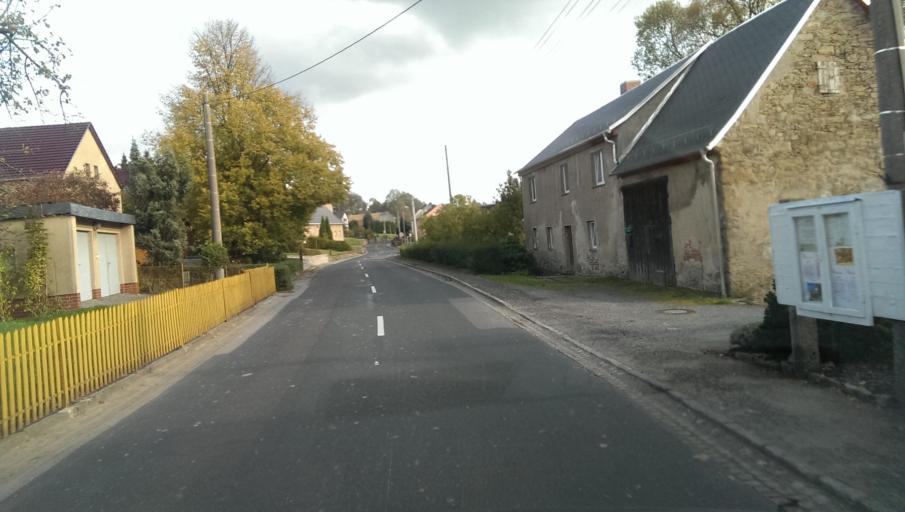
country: DE
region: Saxony
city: Haselbachtal
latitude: 51.2344
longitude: 14.0452
